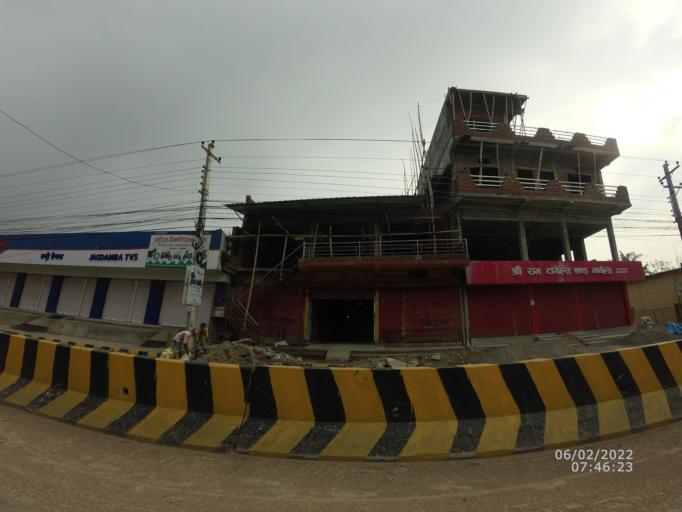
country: NP
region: Western Region
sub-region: Lumbini Zone
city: Bhairahawa
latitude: 27.5184
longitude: 83.4511
